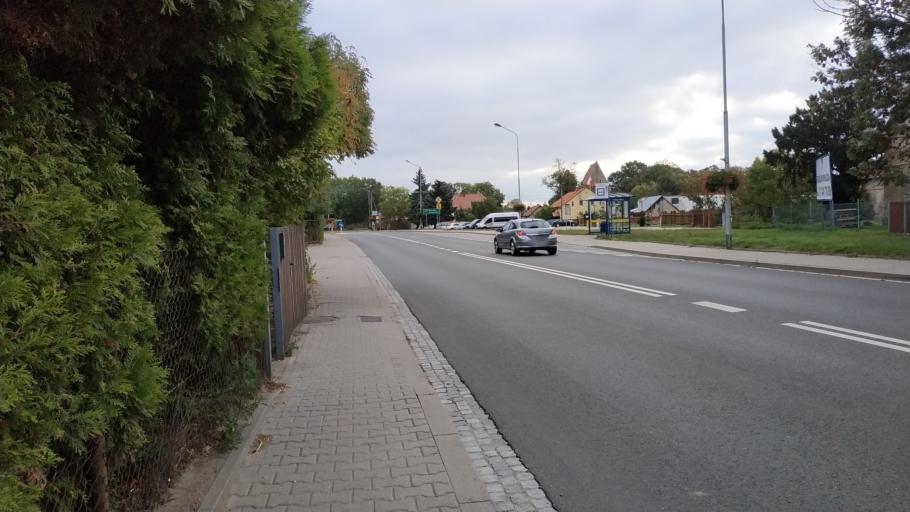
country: PL
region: Lower Silesian Voivodeship
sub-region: Powiat wroclawski
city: Tyniec Maly
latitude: 51.0188
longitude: 16.9180
